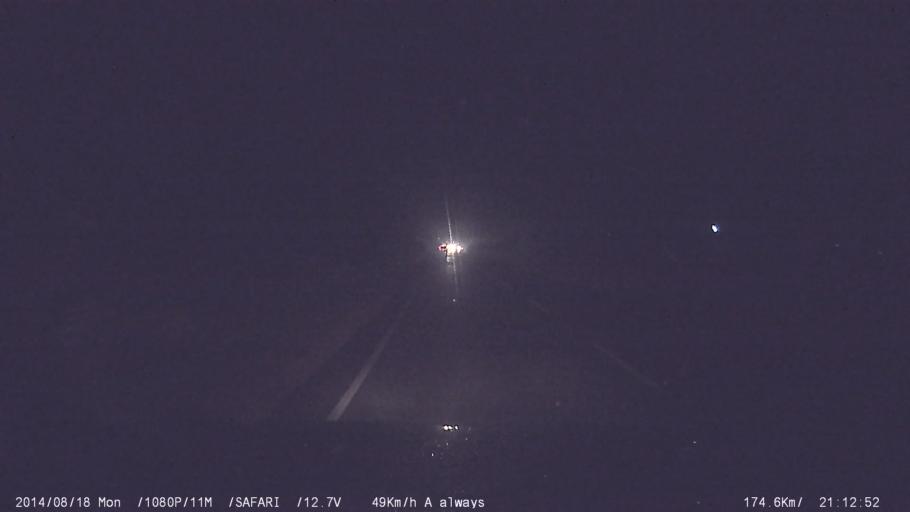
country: IN
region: Kerala
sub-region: Thrissur District
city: Trichur
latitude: 10.5481
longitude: 76.3015
